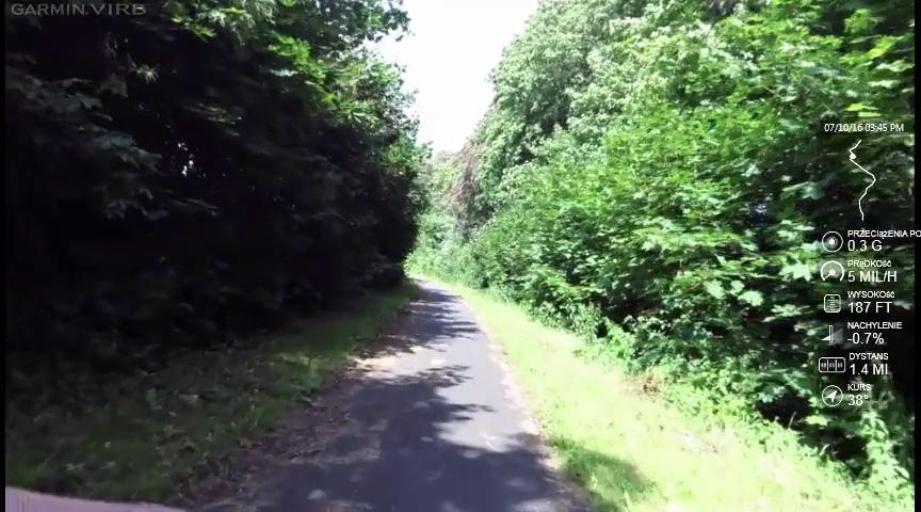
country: PL
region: West Pomeranian Voivodeship
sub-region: Powiat gryfinski
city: Banie
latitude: 53.1306
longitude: 14.6174
